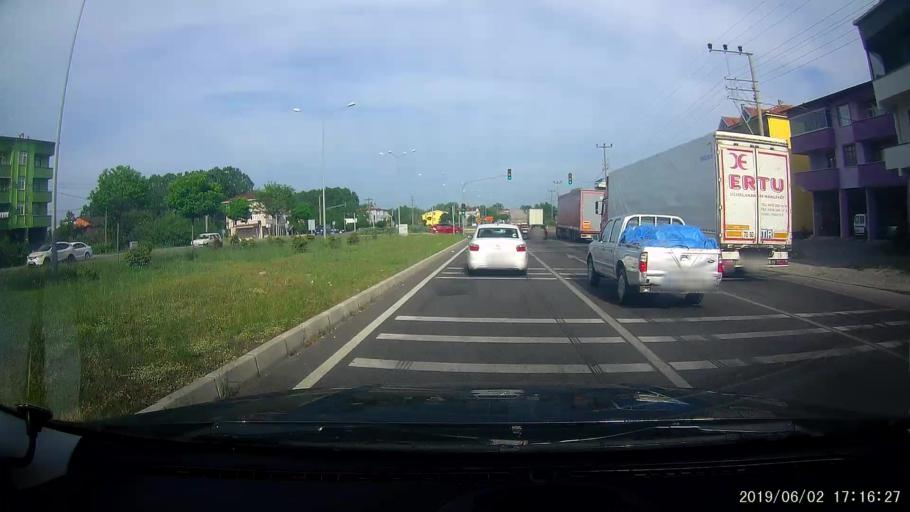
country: TR
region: Samsun
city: Dikbiyik
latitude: 41.2341
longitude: 36.5673
